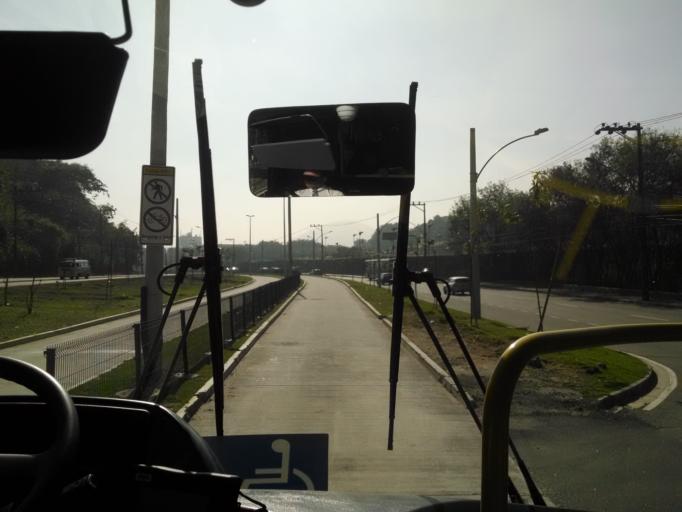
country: BR
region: Rio de Janeiro
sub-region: Sao Joao De Meriti
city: Sao Joao de Meriti
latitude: -22.9083
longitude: -43.3584
